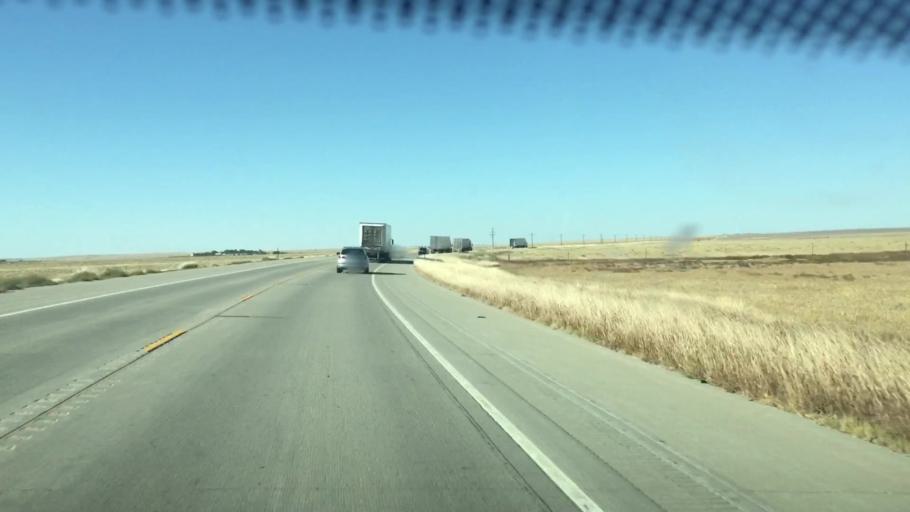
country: US
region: Colorado
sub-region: Kiowa County
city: Eads
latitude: 38.3735
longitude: -102.7292
